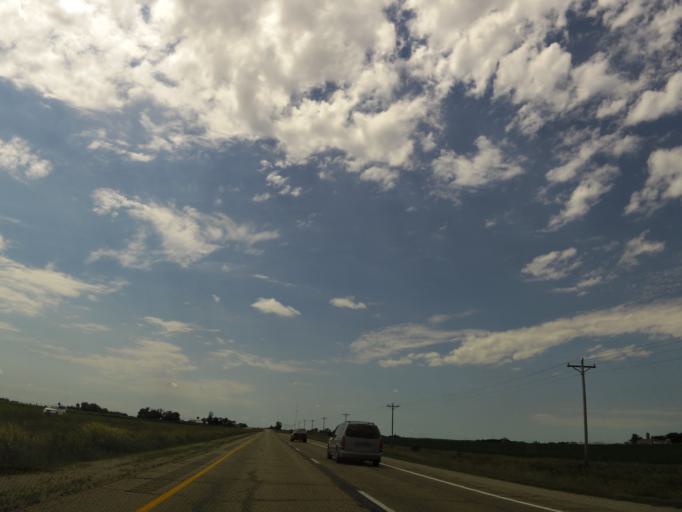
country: US
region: Iowa
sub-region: Bremer County
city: Tripoli
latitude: 42.7951
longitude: -92.3375
